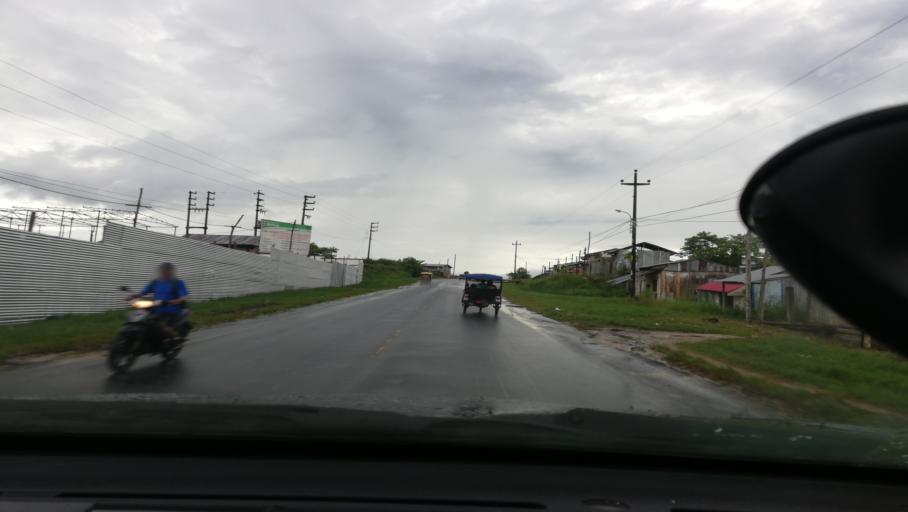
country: PE
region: Loreto
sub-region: Provincia de Maynas
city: Iquitos
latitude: -3.8343
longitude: -73.3285
